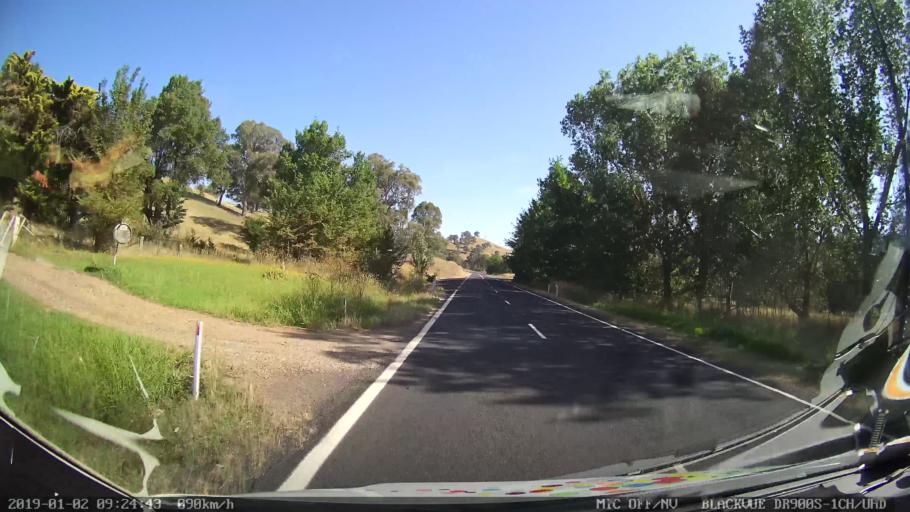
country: AU
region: New South Wales
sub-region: Tumut Shire
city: Tumut
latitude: -35.3734
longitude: 148.2918
